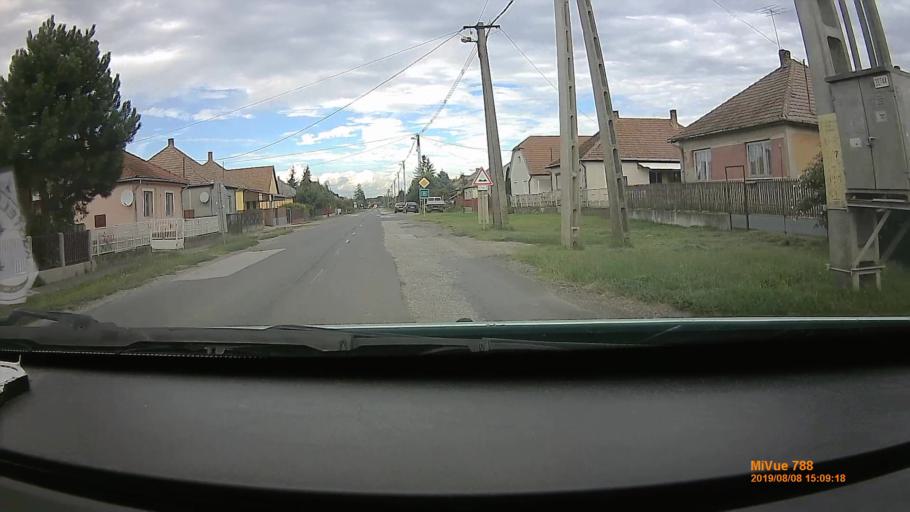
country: HU
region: Szabolcs-Szatmar-Bereg
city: Tunyogmatolcs
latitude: 47.9635
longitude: 22.4460
